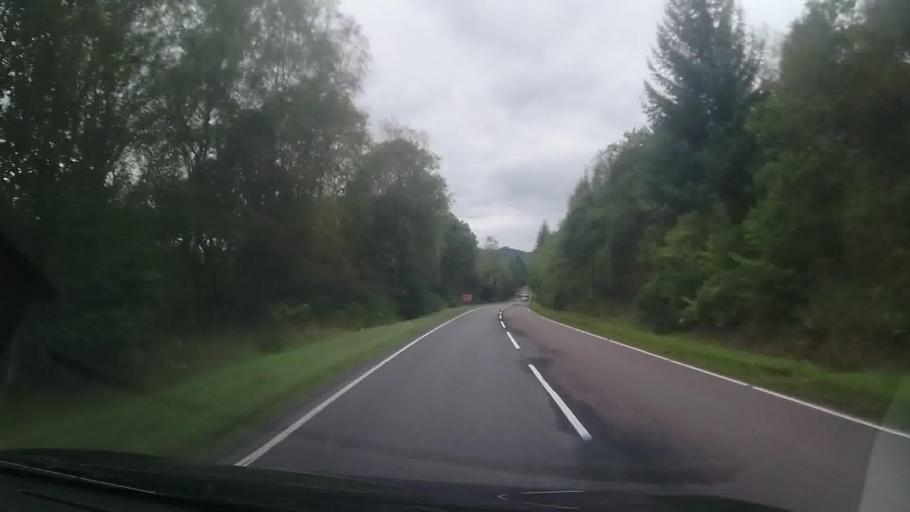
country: GB
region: Scotland
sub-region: Argyll and Bute
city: Garelochhead
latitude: 56.2585
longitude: -5.0877
